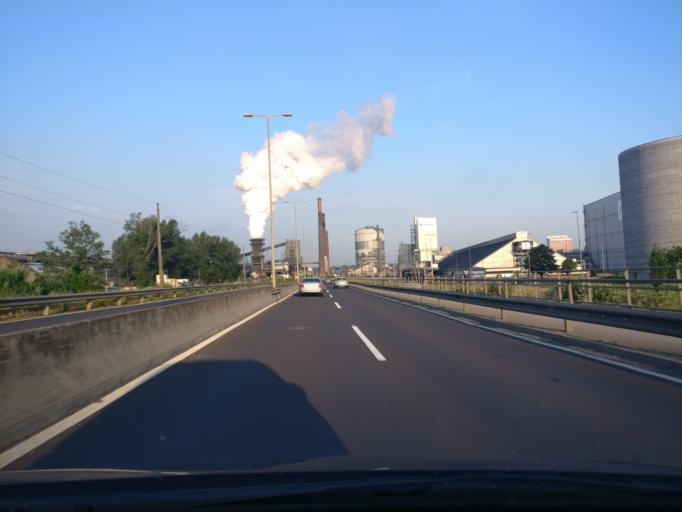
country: AT
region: Upper Austria
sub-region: Politischer Bezirk Urfahr-Umgebung
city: Steyregg
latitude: 48.2859
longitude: 14.3381
